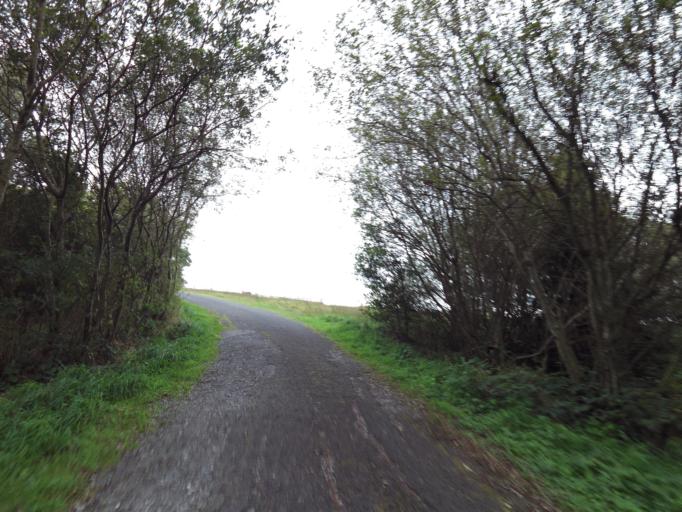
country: IE
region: Leinster
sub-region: Uibh Fhaili
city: Ferbane
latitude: 53.2114
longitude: -7.7306
